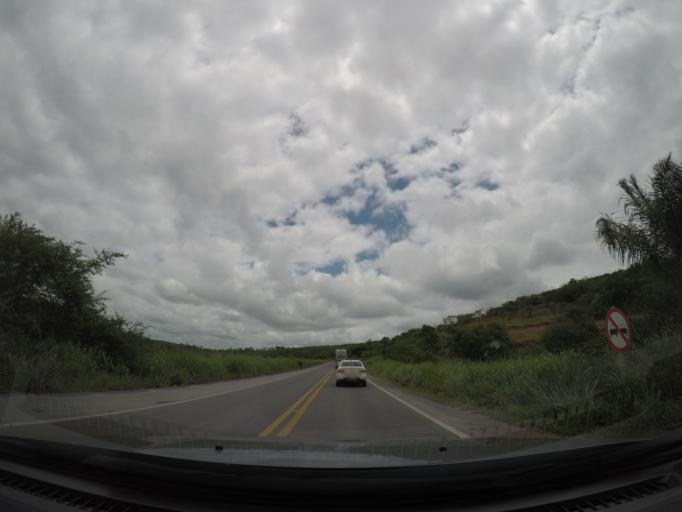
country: BR
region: Bahia
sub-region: Ruy Barbosa
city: Terra Nova
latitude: -12.4593
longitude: -40.5701
